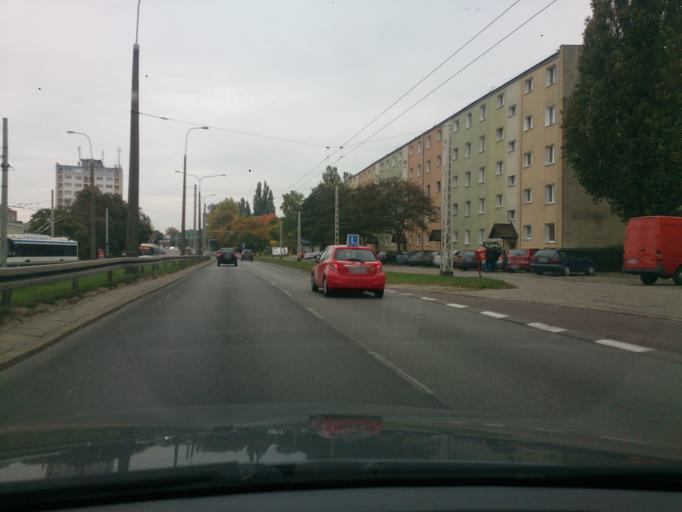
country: PL
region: Pomeranian Voivodeship
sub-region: Gdynia
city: Pogorze
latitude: 54.5353
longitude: 18.4805
